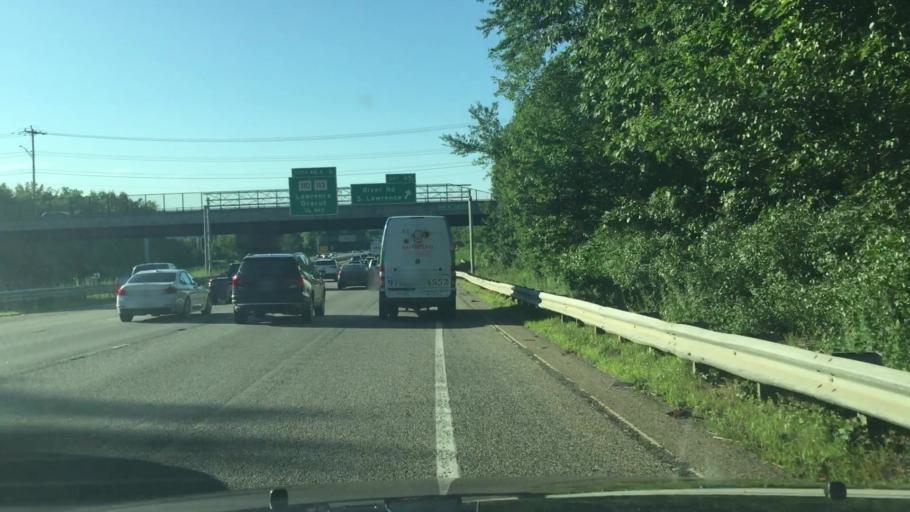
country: US
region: Massachusetts
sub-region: Essex County
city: Methuen
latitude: 42.6897
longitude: -71.2057
